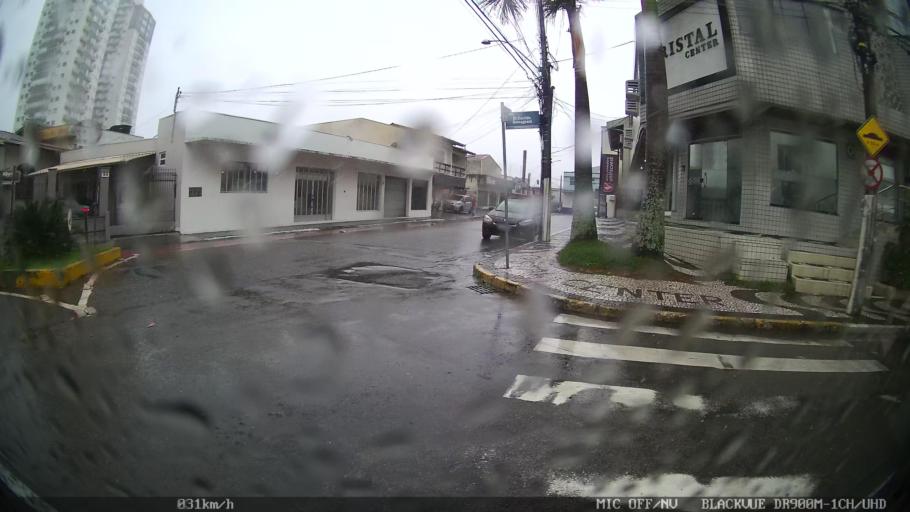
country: BR
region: Santa Catarina
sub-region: Itajai
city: Itajai
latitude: -26.9064
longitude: -48.6640
